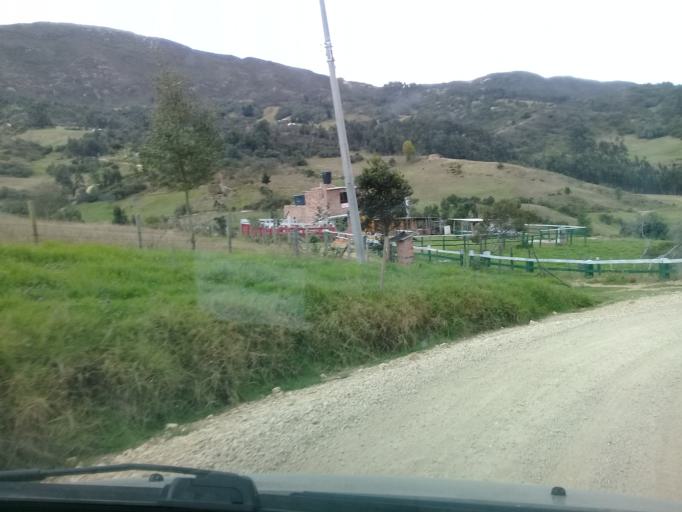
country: CO
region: Cundinamarca
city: Lenguazaque
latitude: 5.2903
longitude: -73.7257
